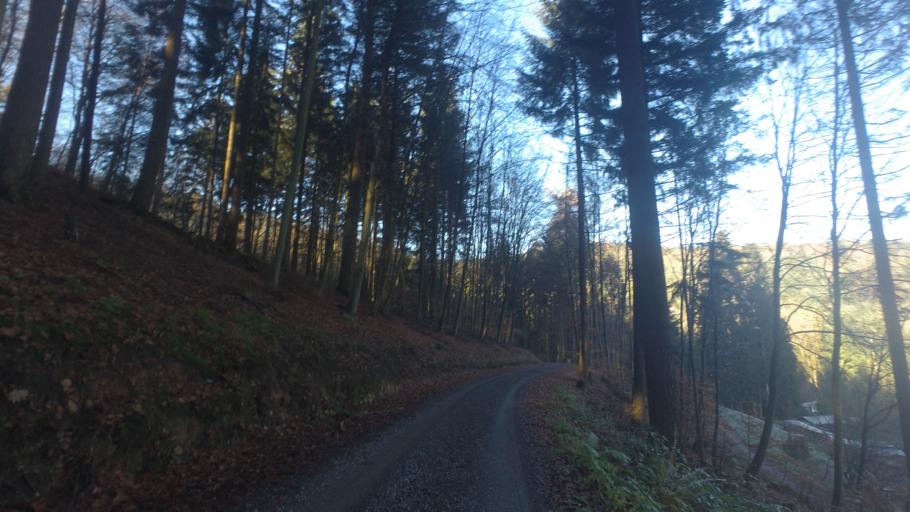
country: DE
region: Baden-Wuerttemberg
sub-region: Karlsruhe Region
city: Heiligkreuzsteinach
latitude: 49.5000
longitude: 8.8052
